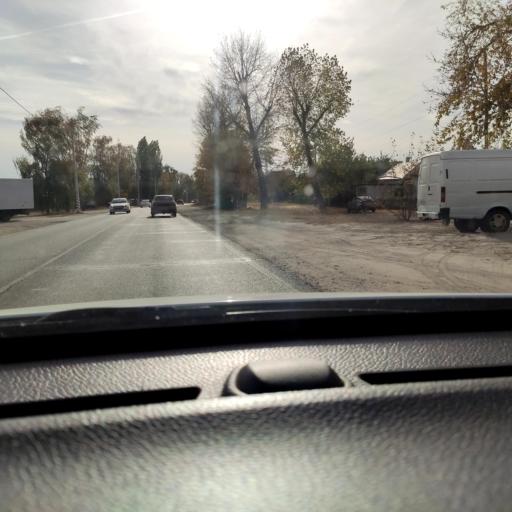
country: RU
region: Voronezj
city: Maslovka
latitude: 51.5597
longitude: 39.2430
